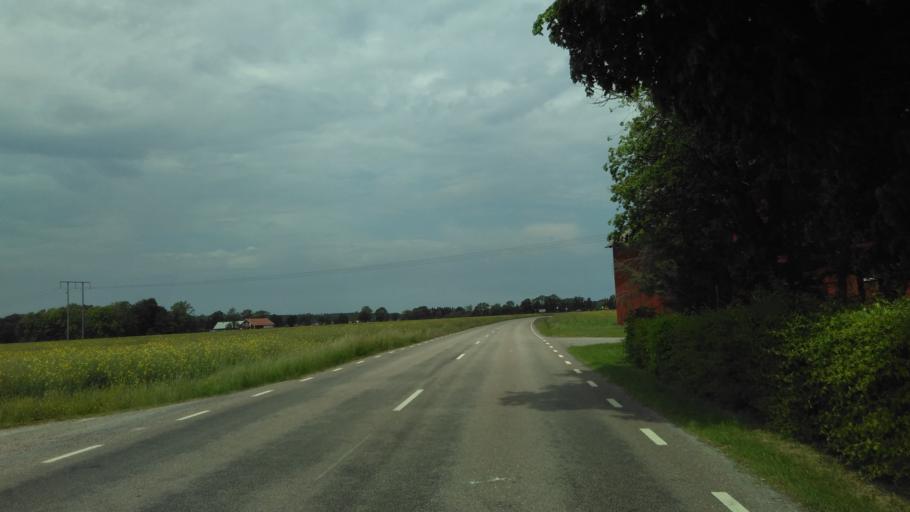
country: SE
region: Vaestra Goetaland
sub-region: Lidkopings Kommun
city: Lidkoping
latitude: 58.4714
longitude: 13.1406
